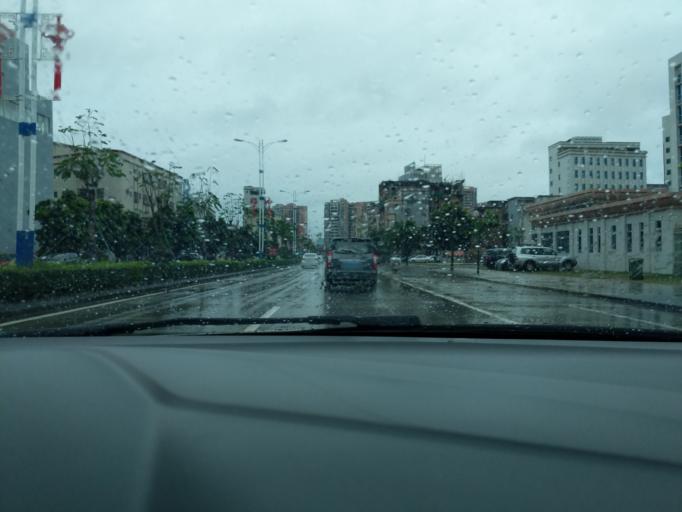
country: CN
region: Guangdong
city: Pingshi
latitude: 22.1991
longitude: 112.3315
